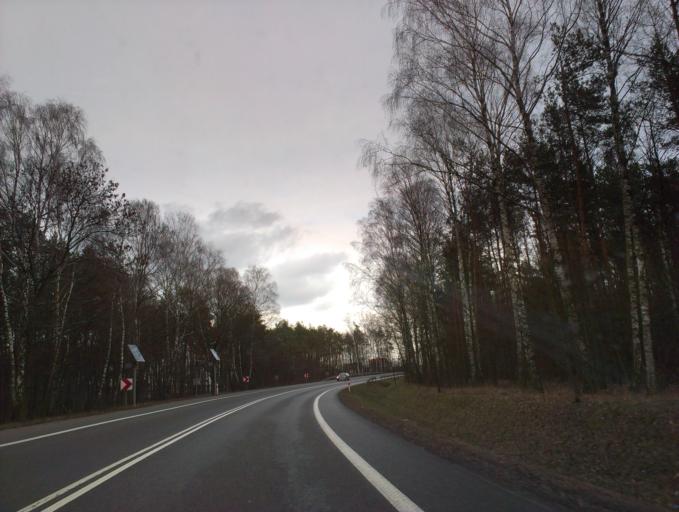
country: PL
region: Masovian Voivodeship
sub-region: Powiat sierpecki
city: Sierpc
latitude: 52.8711
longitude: 19.6394
